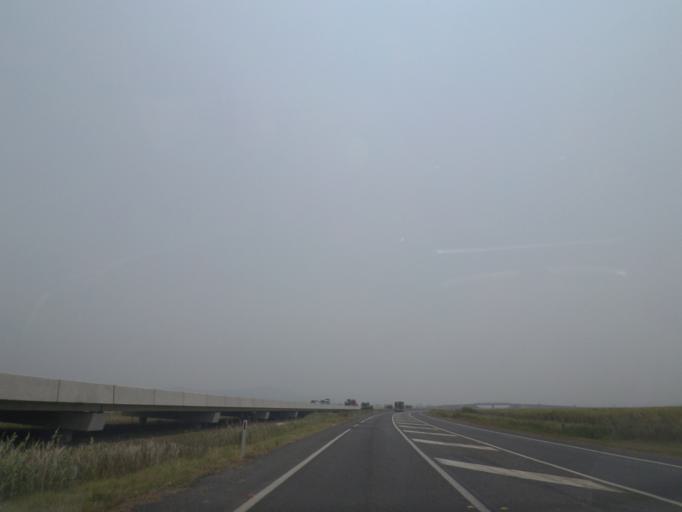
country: AU
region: New South Wales
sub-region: Clarence Valley
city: Maclean
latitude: -29.3995
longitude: 153.2401
